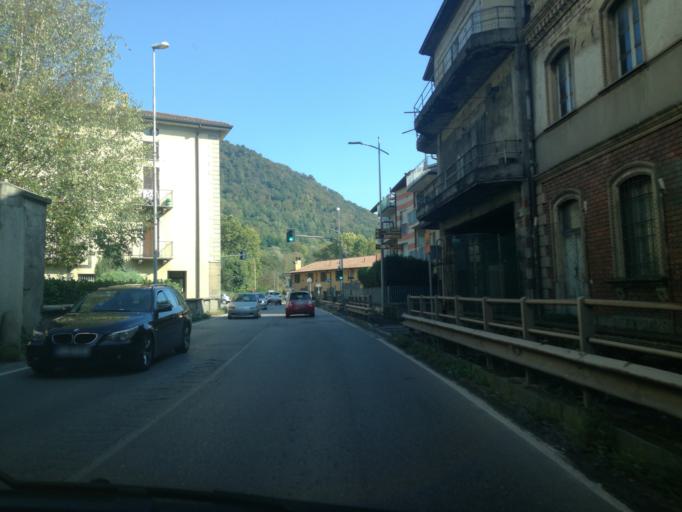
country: IT
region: Lombardy
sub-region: Provincia di Bergamo
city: Cisano Bergamasco
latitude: 45.7389
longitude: 9.4833
